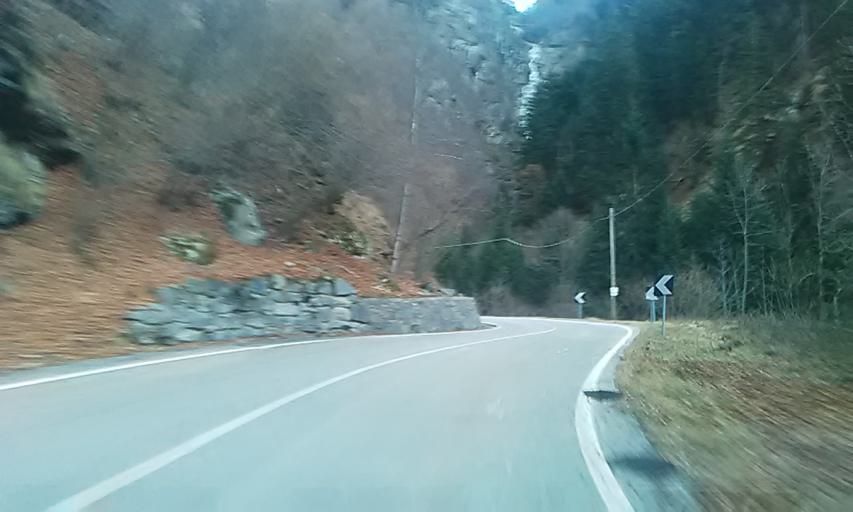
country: IT
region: Piedmont
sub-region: Provincia di Vercelli
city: Rimasco
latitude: 45.8667
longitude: 8.0686
